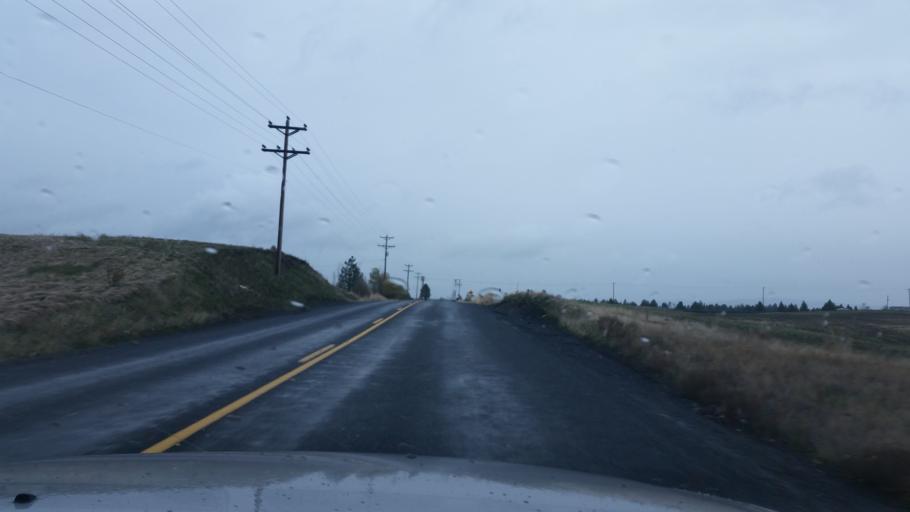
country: US
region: Washington
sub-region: Spokane County
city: Airway Heights
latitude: 47.6682
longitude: -117.6038
